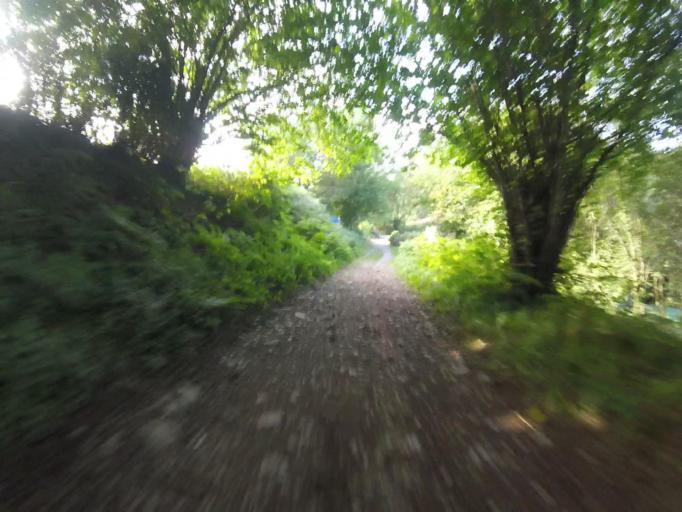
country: ES
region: Basque Country
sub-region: Provincia de Guipuzcoa
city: Irun
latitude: 43.3203
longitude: -1.7546
